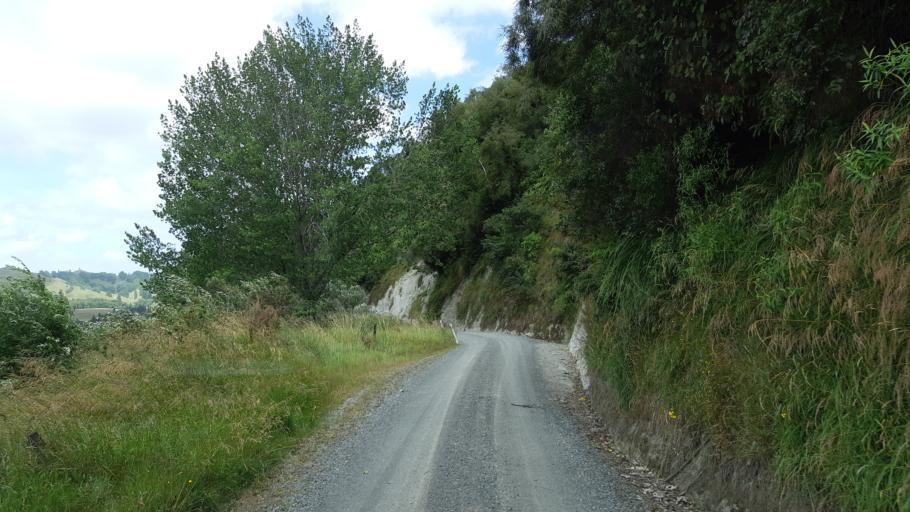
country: NZ
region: Manawatu-Wanganui
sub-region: Ruapehu District
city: Waiouru
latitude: -39.7807
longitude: 175.9076
